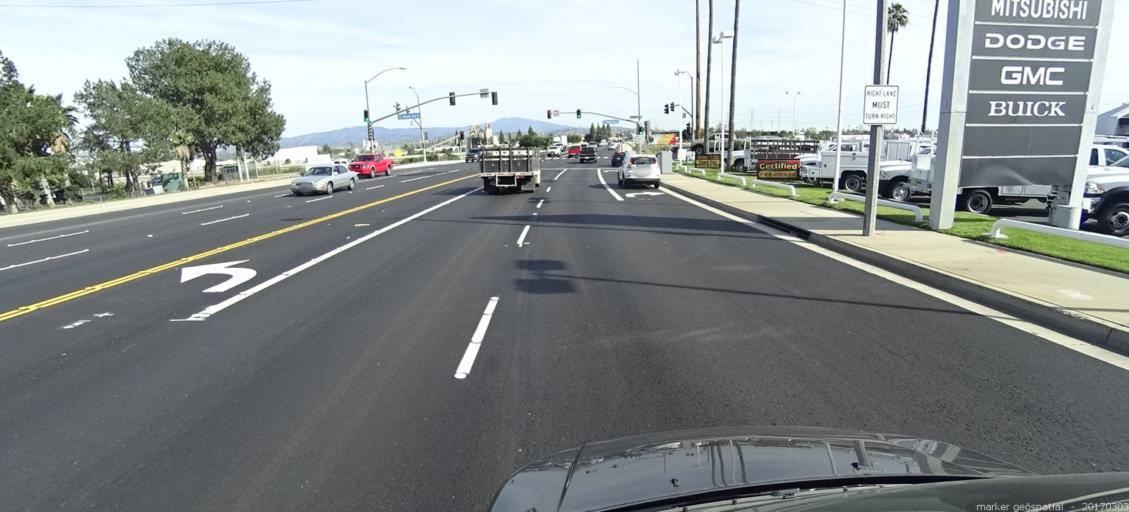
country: US
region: California
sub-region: Orange County
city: Orange
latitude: 33.8178
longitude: -117.8730
